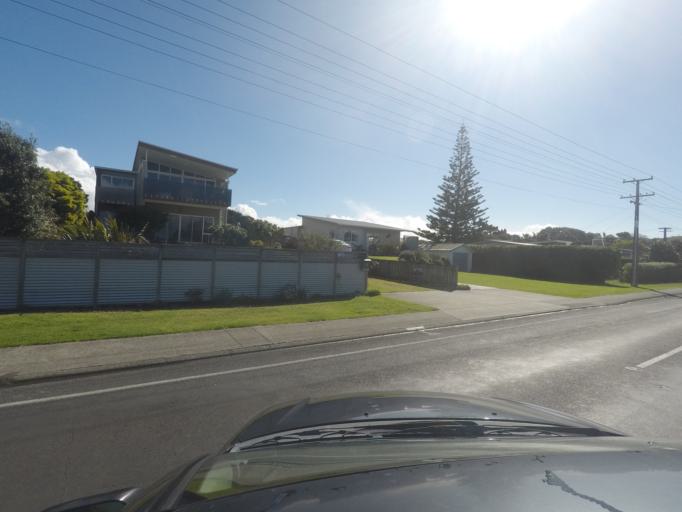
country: NZ
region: Bay of Plenty
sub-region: Western Bay of Plenty District
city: Waihi Beach
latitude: -37.4192
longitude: 175.9502
